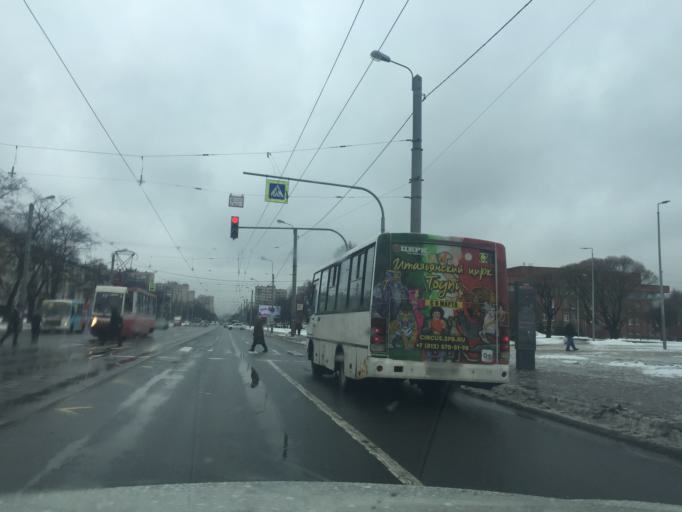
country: RU
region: Leningrad
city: Akademicheskoe
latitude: 60.0045
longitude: 30.4316
